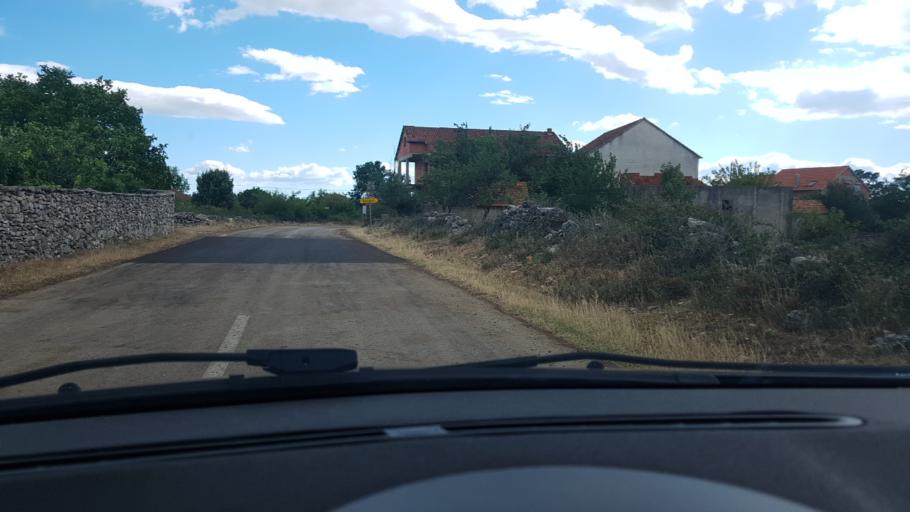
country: HR
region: Sibensko-Kniniska
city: Kistanje
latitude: 44.0572
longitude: 15.9268
